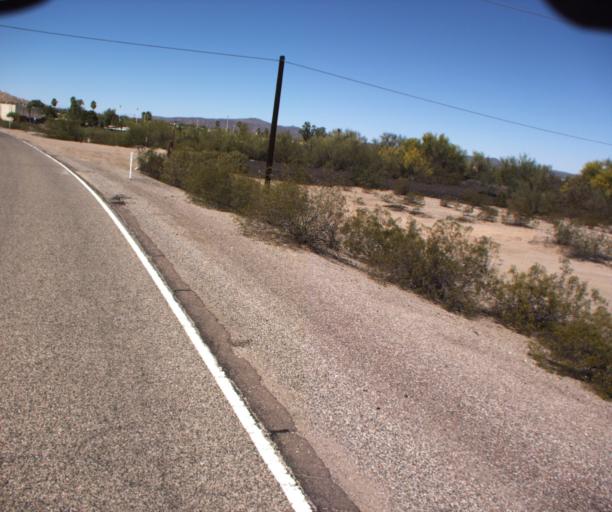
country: US
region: Arizona
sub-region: Pima County
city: Ajo
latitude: 32.3720
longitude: -112.8557
